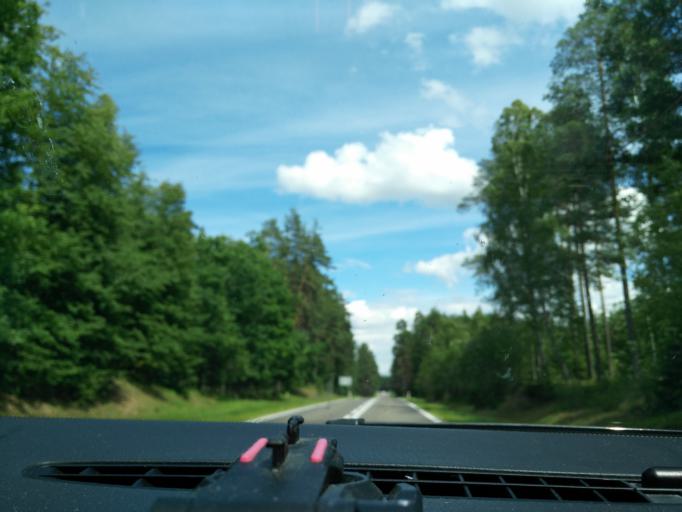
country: PL
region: Podlasie
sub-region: Powiat sejnenski
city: Sejny
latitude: 53.9776
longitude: 23.2810
